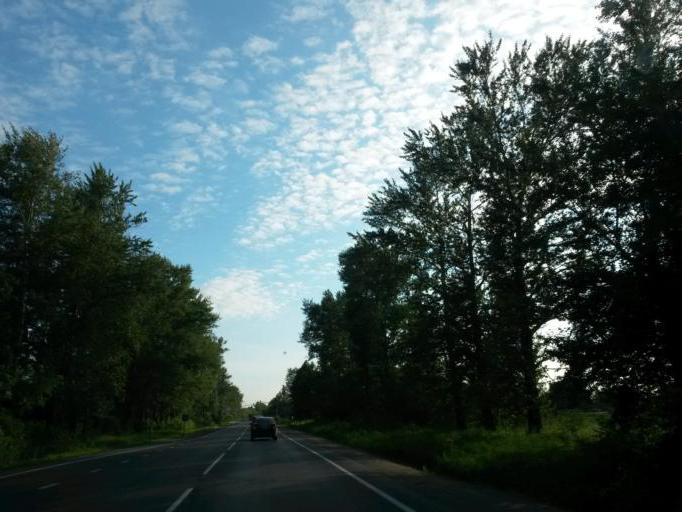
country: RU
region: Moskovskaya
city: Yam
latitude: 55.4557
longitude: 37.6795
